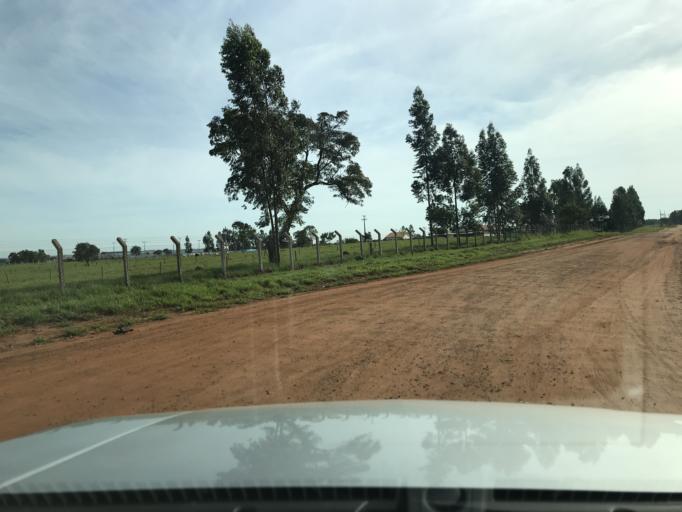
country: BR
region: Mato Grosso do Sul
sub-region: Iguatemi
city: Iguatemi
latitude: -23.6622
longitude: -54.5691
